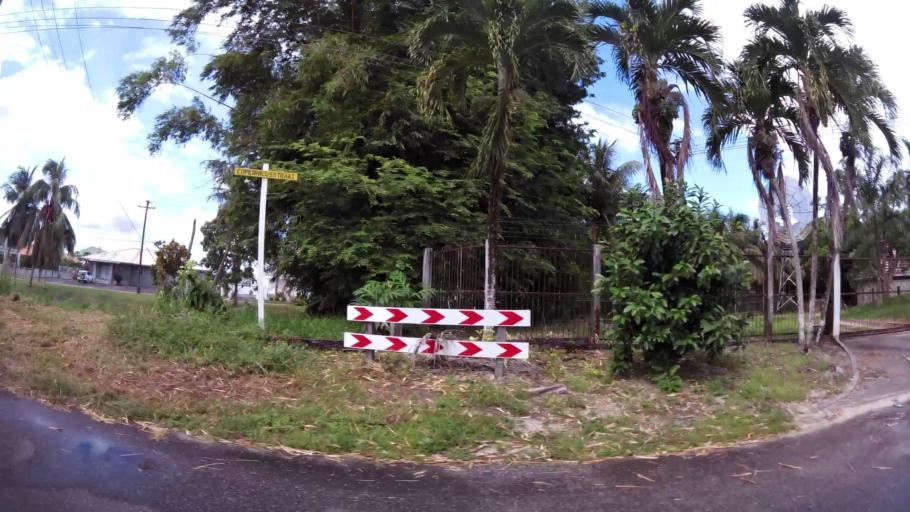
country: SR
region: Paramaribo
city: Paramaribo
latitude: 5.8378
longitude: -55.1250
